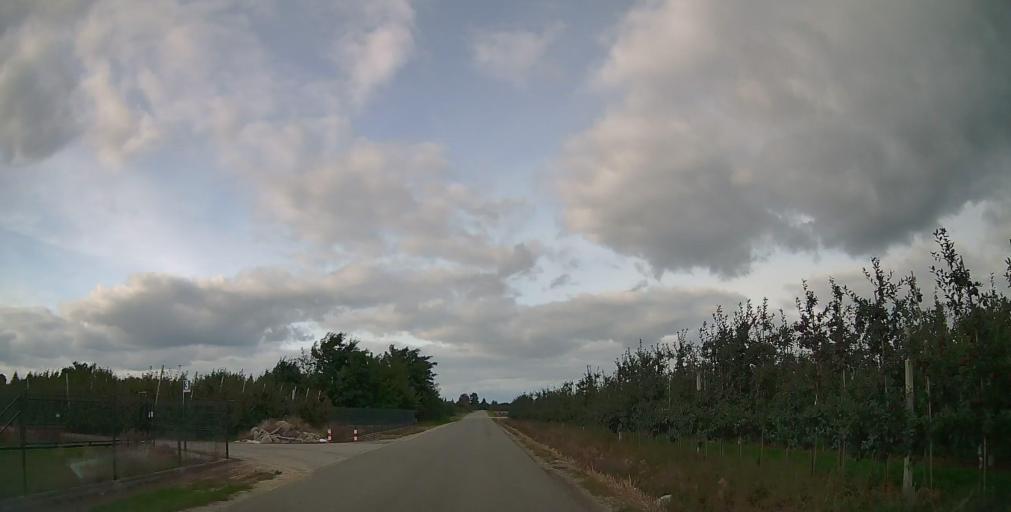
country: PL
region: Masovian Voivodeship
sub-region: Powiat bialobrzeski
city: Promna
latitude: 51.7184
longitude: 20.9585
